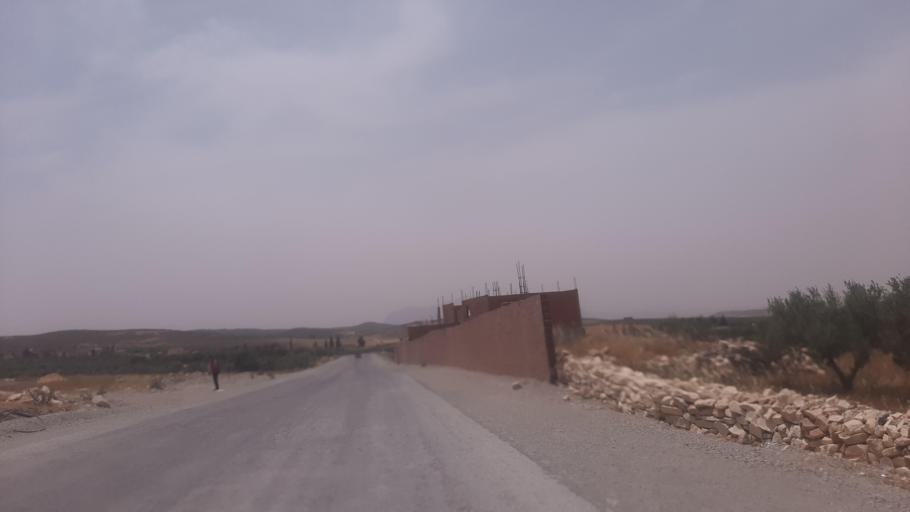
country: TN
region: Zaghwan
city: Zaghouan
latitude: 36.5243
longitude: 10.1586
